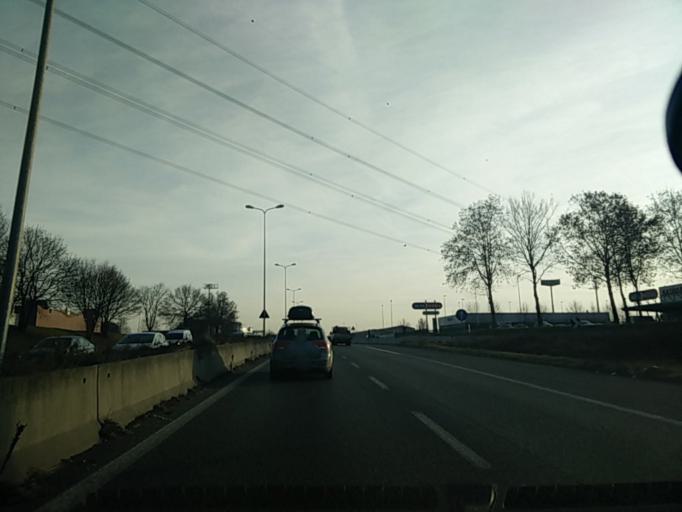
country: IT
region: Lombardy
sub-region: Provincia di Monza e Brianza
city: Varedo
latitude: 45.5958
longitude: 9.1722
